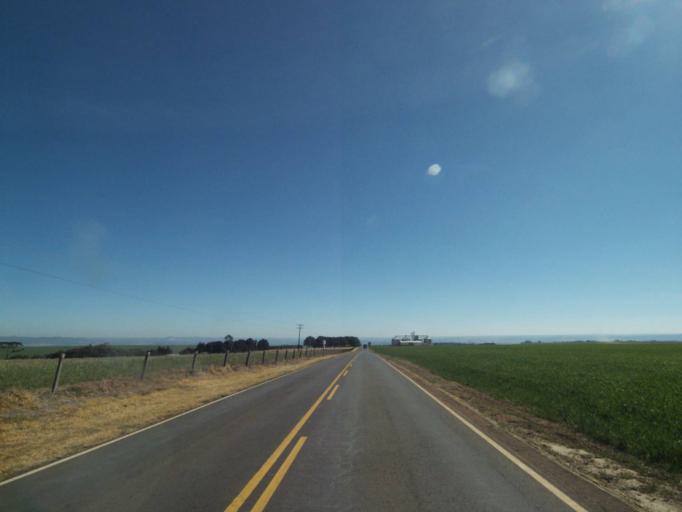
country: BR
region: Parana
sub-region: Tibagi
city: Tibagi
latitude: -24.5449
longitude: -50.3008
